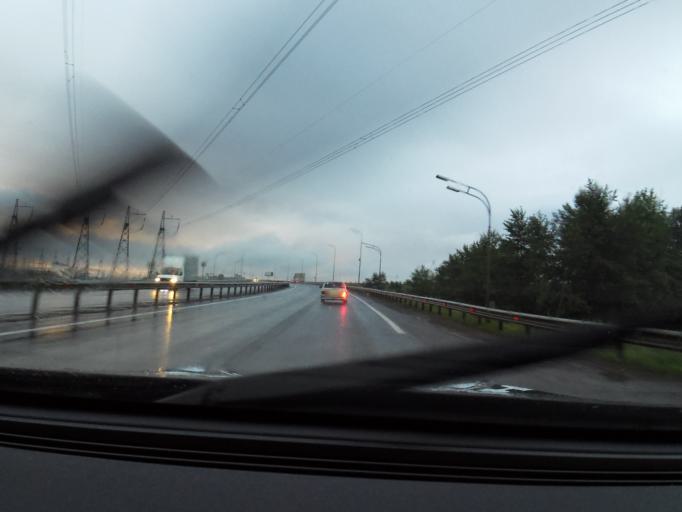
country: RU
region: Tatarstan
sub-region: Tukayevskiy Rayon
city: Naberezhnyye Chelny
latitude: 55.6876
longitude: 52.2829
